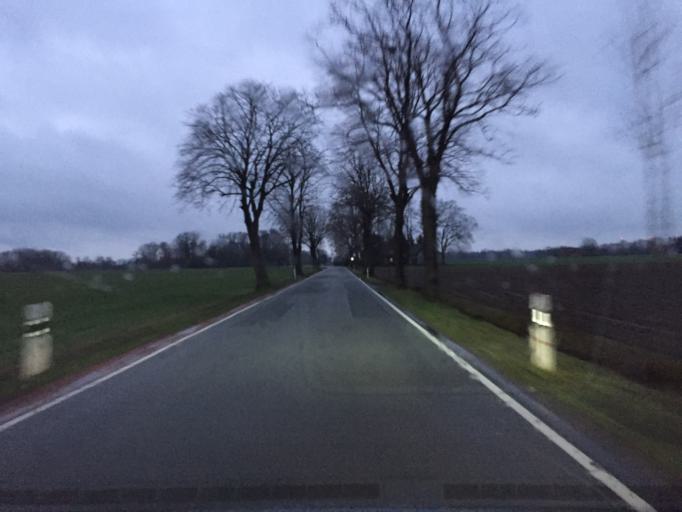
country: DE
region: Lower Saxony
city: Sudwalde
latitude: 52.7847
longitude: 8.8334
